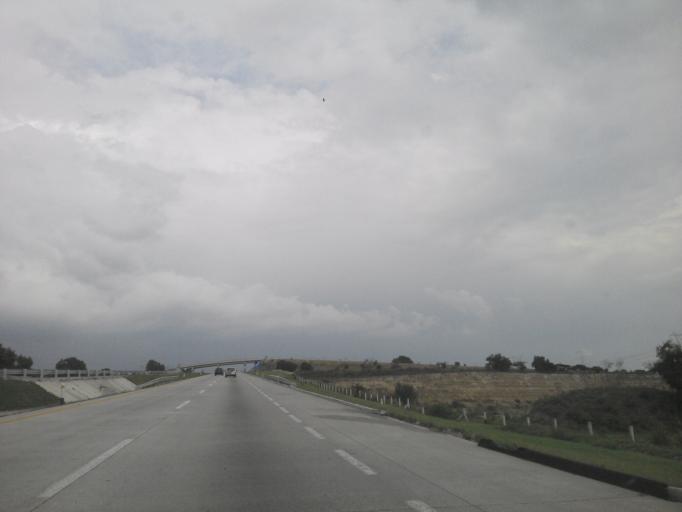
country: MX
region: Mexico
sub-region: Apaxco
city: Colonia Juarez
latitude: 19.9820
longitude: -99.1192
